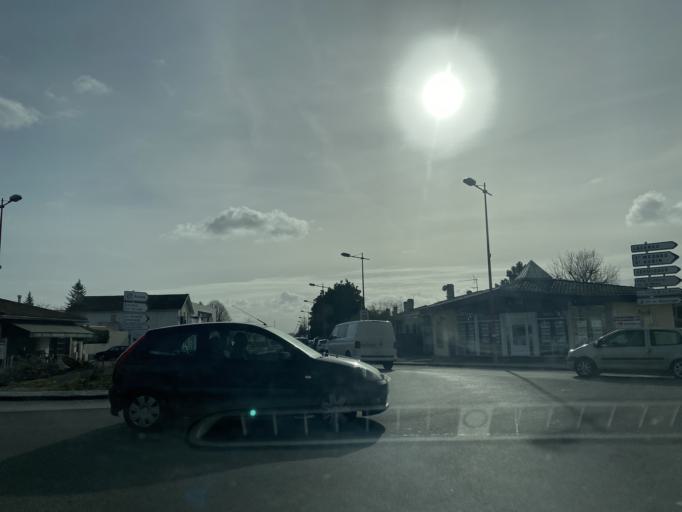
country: FR
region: Aquitaine
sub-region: Departement de la Gironde
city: Le Taillan-Medoc
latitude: 44.9092
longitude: -0.6689
